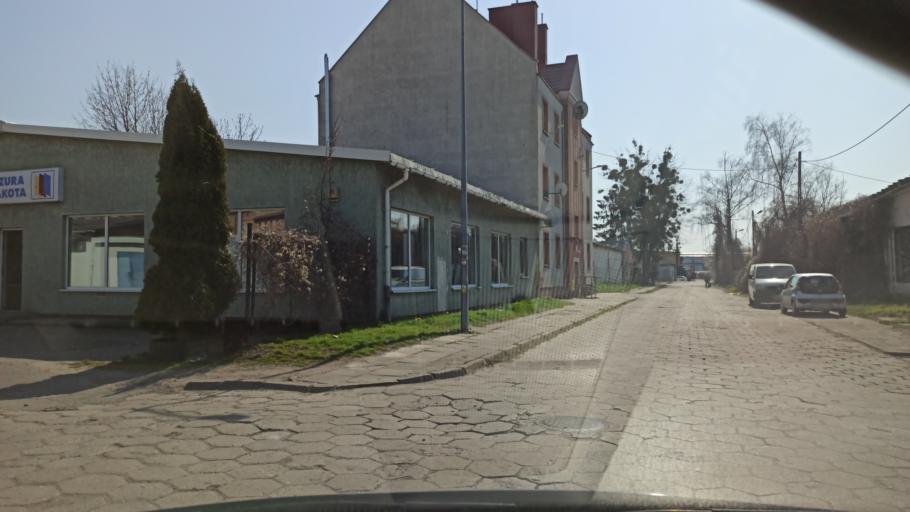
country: PL
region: Warmian-Masurian Voivodeship
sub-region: Powiat elblaski
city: Elblag
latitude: 54.1521
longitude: 19.3999
